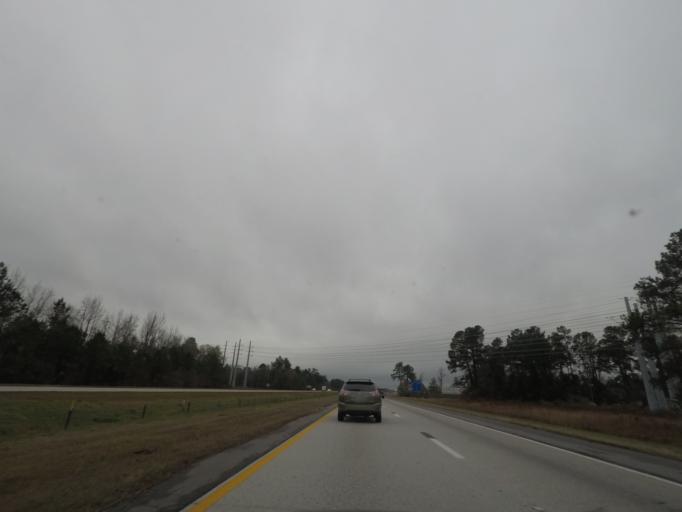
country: US
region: South Carolina
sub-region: Dorchester County
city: Saint George
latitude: 33.2109
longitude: -80.5995
